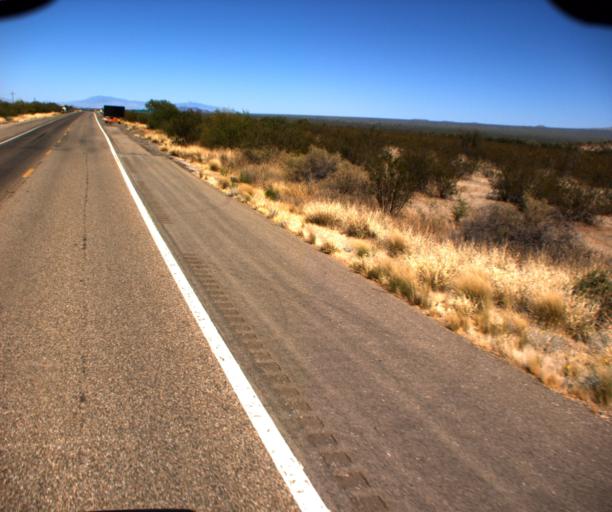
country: US
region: Arizona
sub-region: Pima County
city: Three Points
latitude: 32.0617
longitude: -111.3901
